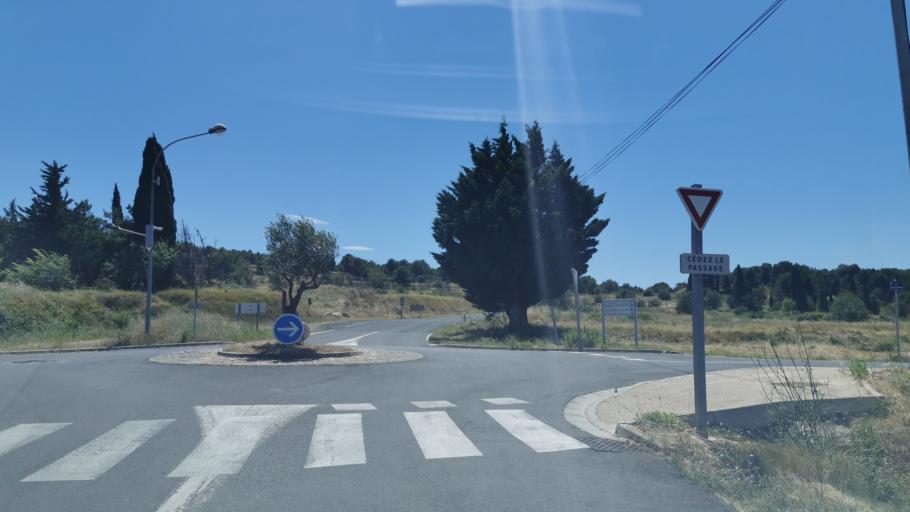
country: FR
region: Languedoc-Roussillon
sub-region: Departement de l'Herault
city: Nissan-lez-Enserune
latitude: 43.2829
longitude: 3.1229
